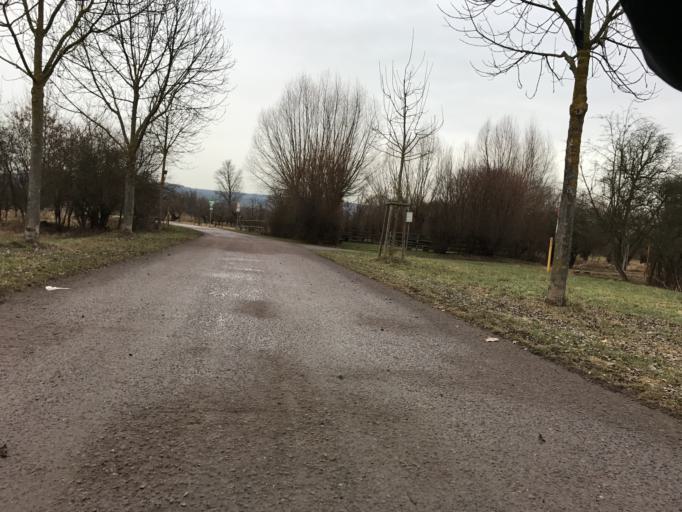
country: DE
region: Hesse
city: Geisenheim
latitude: 49.9684
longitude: 7.9615
